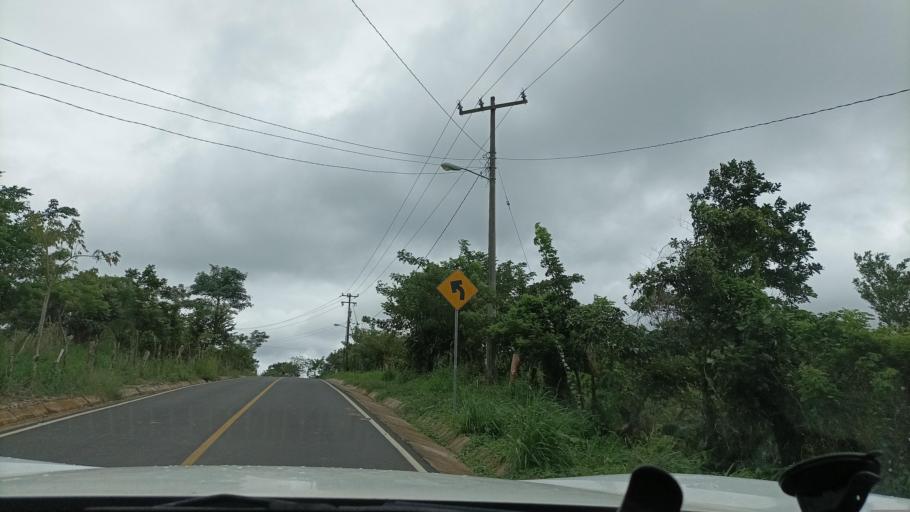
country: MX
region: Veracruz
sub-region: Moloacan
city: Cuichapa
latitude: 17.8081
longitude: -94.3559
